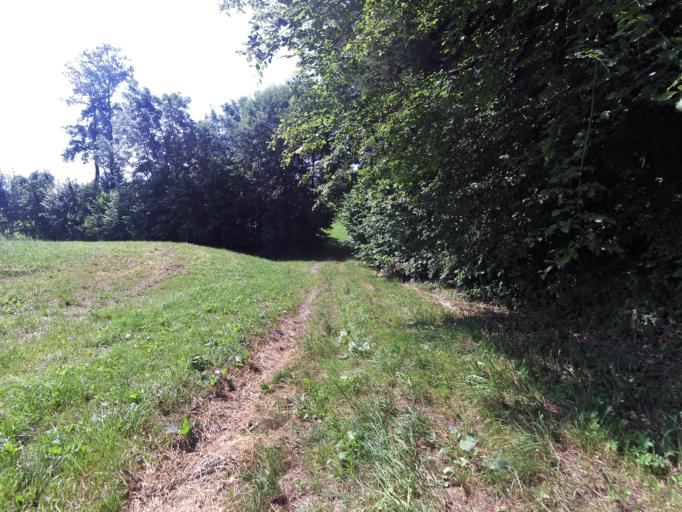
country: CH
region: Thurgau
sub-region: Frauenfeld District
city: Mullheim
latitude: 47.5732
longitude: 8.9950
